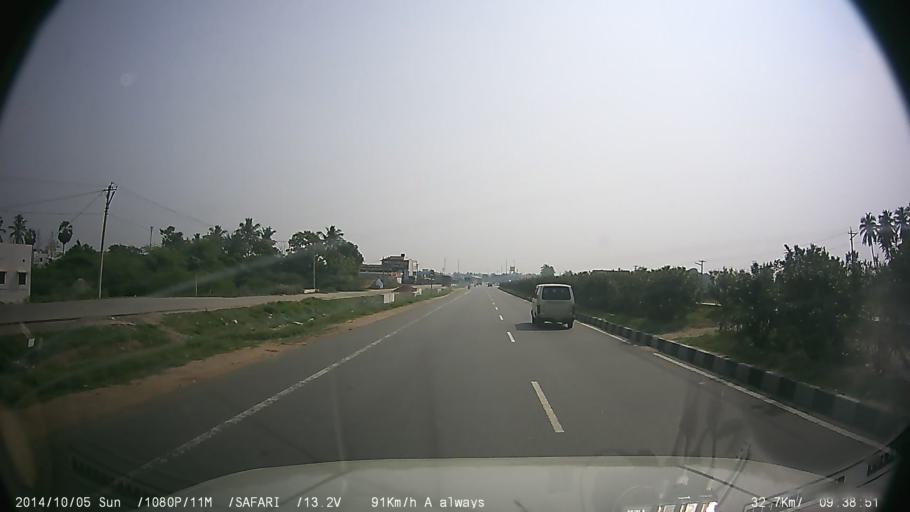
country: IN
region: Tamil Nadu
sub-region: Erode
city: Bhavani
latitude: 11.4362
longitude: 77.7040
